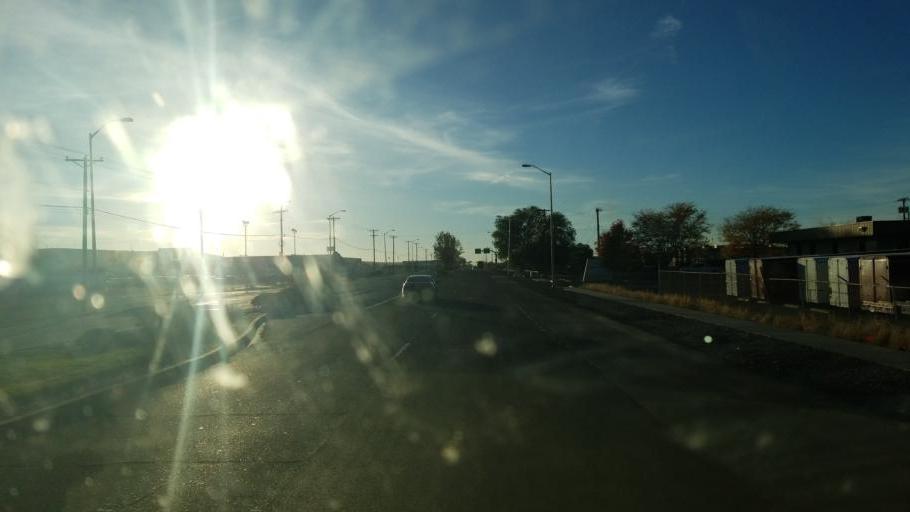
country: US
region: New Mexico
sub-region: San Juan County
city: Farmington
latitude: 36.7194
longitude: -108.1771
